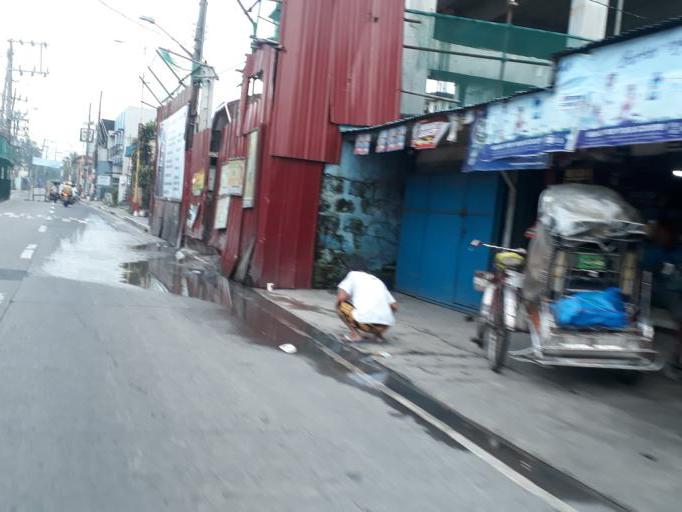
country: PH
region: Calabarzon
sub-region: Province of Rizal
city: Navotas
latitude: 14.6619
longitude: 120.9456
